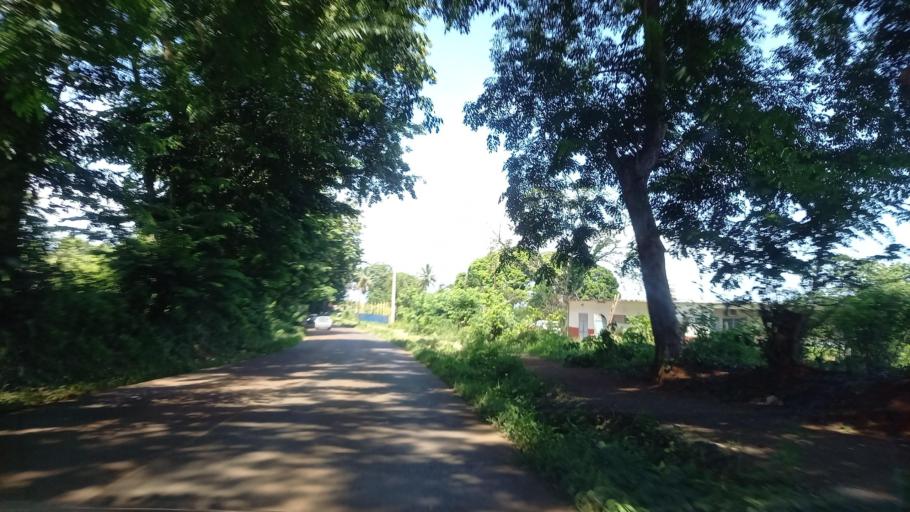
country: YT
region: Tsingoni
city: Tsingoni
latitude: -12.7929
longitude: 45.1191
